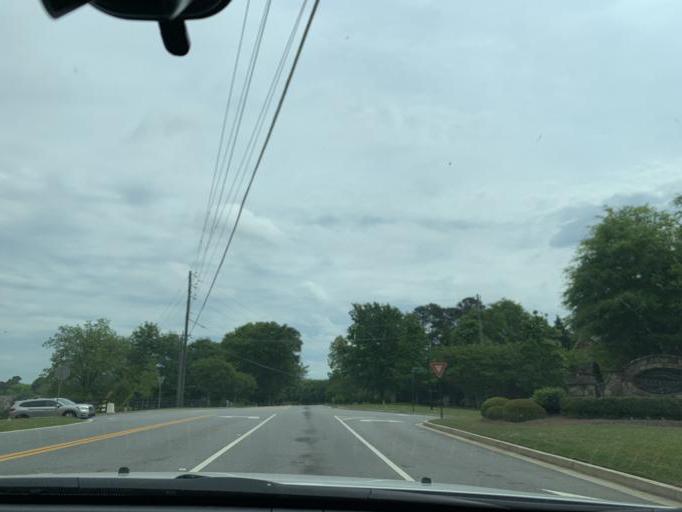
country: US
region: Georgia
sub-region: Forsyth County
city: Cumming
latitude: 34.1422
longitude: -84.2040
